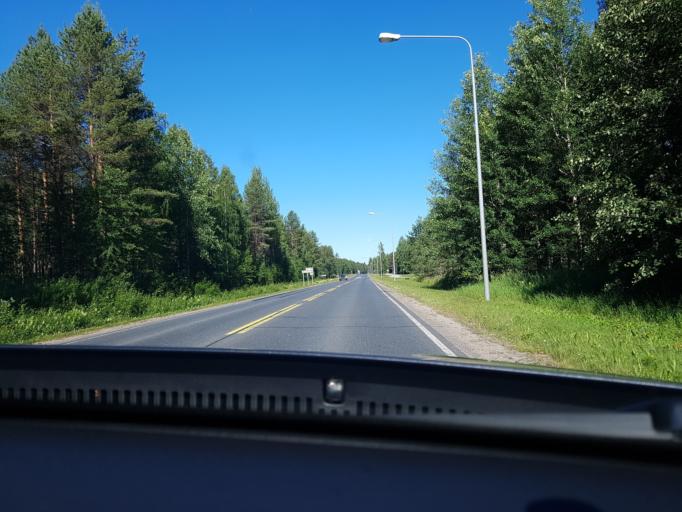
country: FI
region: Kainuu
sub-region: Kehys-Kainuu
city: Kuhmo
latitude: 64.1190
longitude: 29.5248
